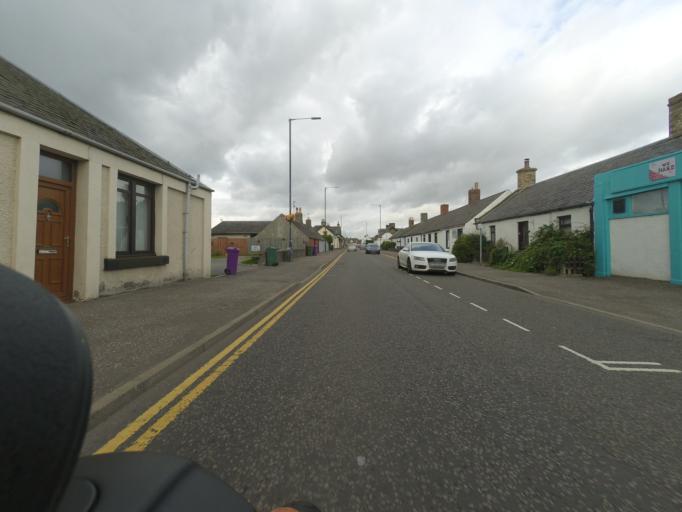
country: GB
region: Scotland
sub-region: Angus
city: Carnoustie
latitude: 56.5007
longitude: -2.7205
